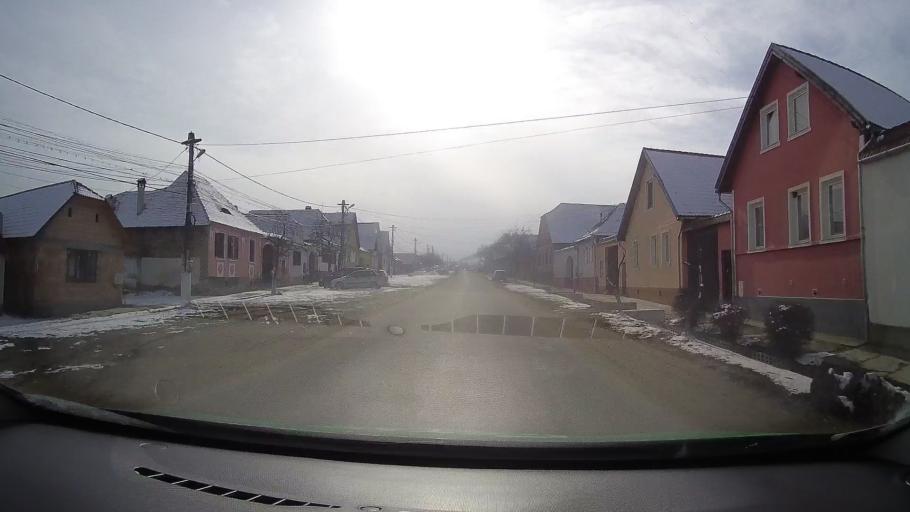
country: RO
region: Sibiu
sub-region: Comuna Laslea
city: Laslea
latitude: 46.2064
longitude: 24.6546
